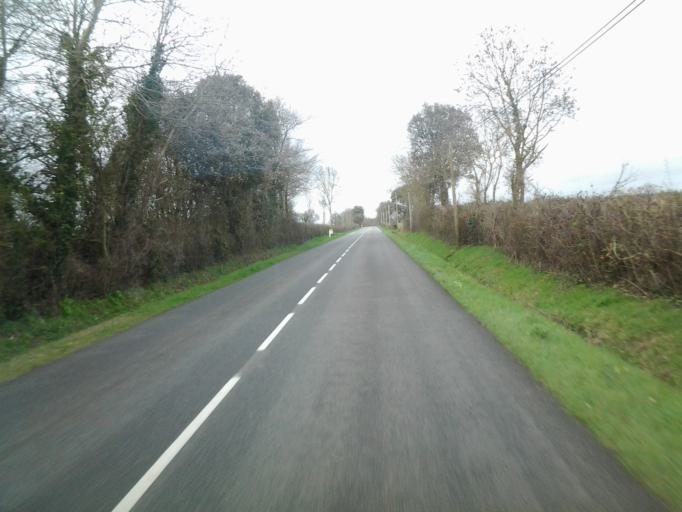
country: FR
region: Pays de la Loire
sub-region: Departement de la Vendee
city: Avrille
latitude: 46.4765
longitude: -1.4828
